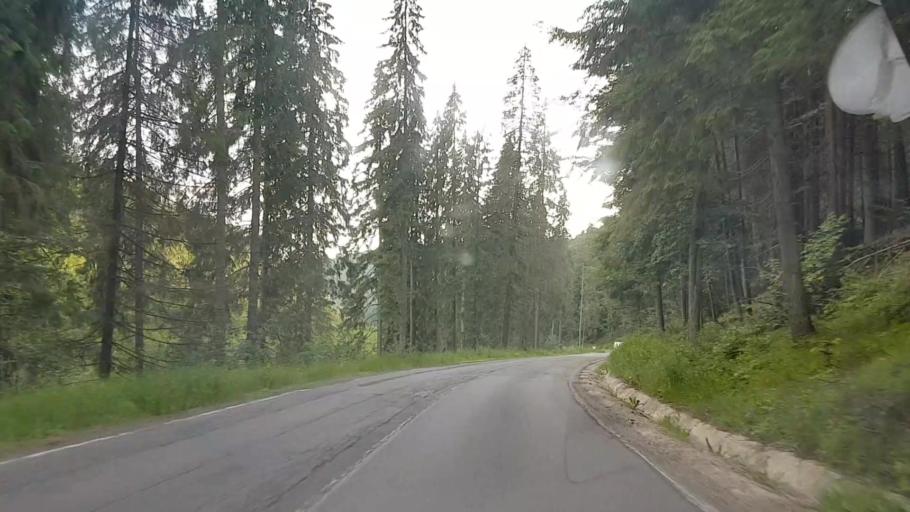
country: RO
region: Harghita
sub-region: Comuna Varsag
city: Varsag
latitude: 46.6409
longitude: 25.2748
